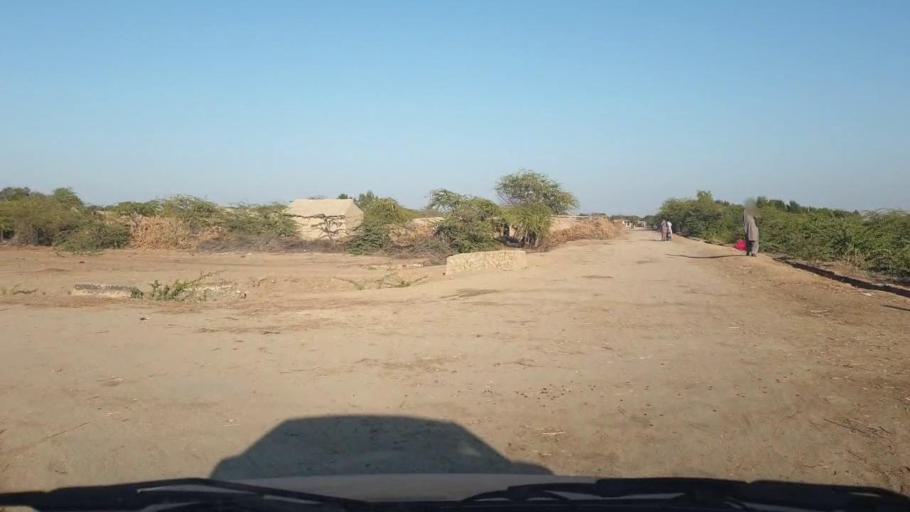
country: PK
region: Sindh
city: Samaro
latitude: 25.3271
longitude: 69.3208
